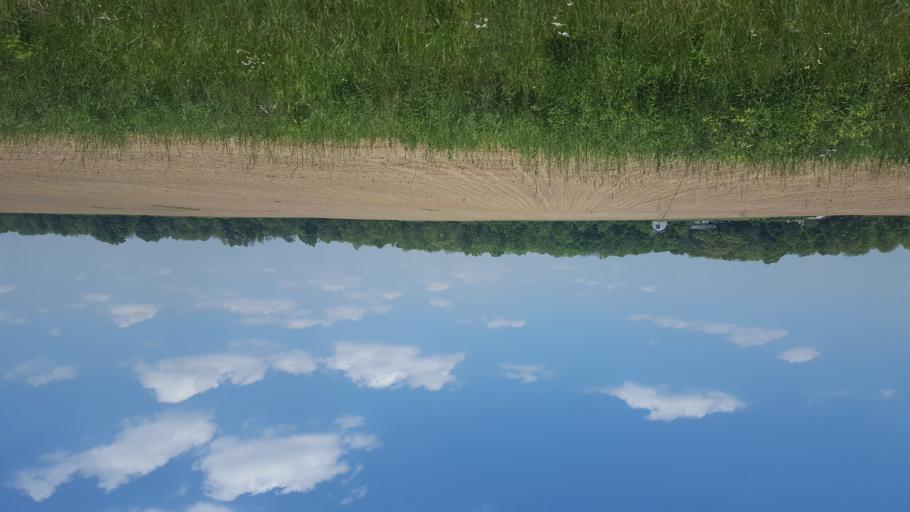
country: US
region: Ohio
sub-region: Knox County
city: Gambier
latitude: 40.2913
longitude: -82.3326
